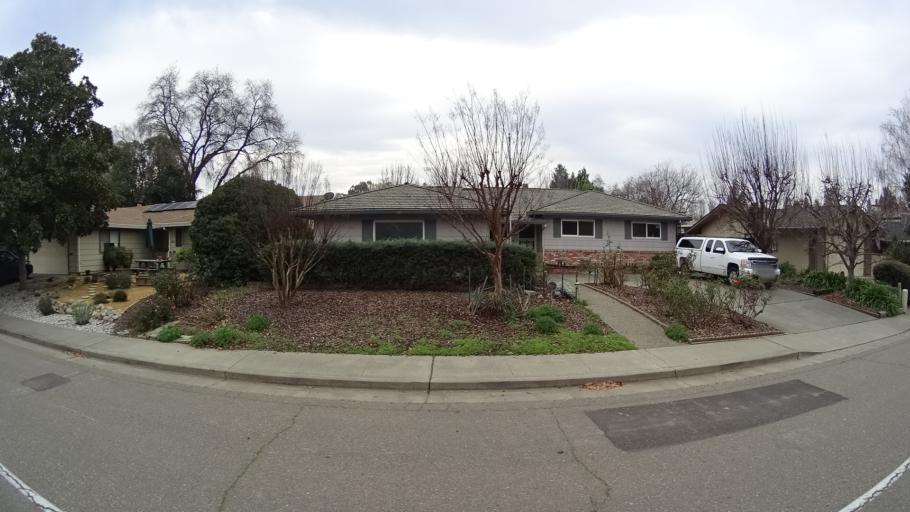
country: US
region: California
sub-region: Yolo County
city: Davis
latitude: 38.5434
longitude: -121.7121
